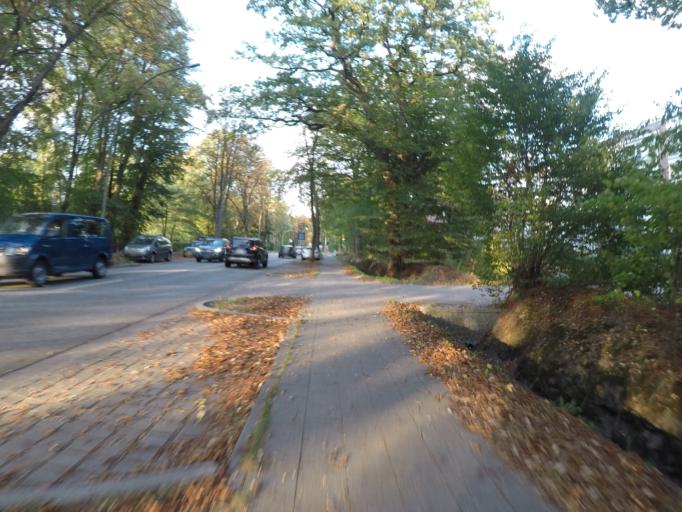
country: DE
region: Hamburg
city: Bergstedt
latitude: 53.6391
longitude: 10.1544
